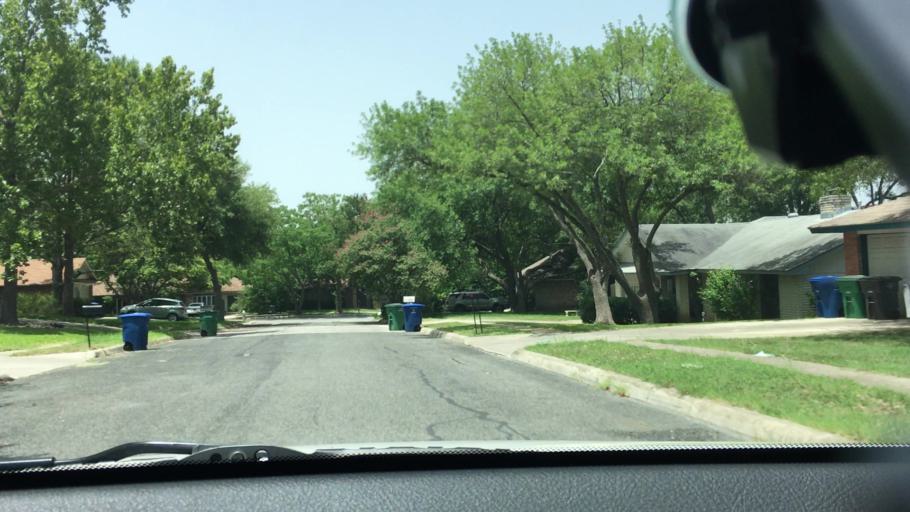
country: US
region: Texas
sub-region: Bexar County
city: Live Oak
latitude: 29.5759
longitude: -98.3645
